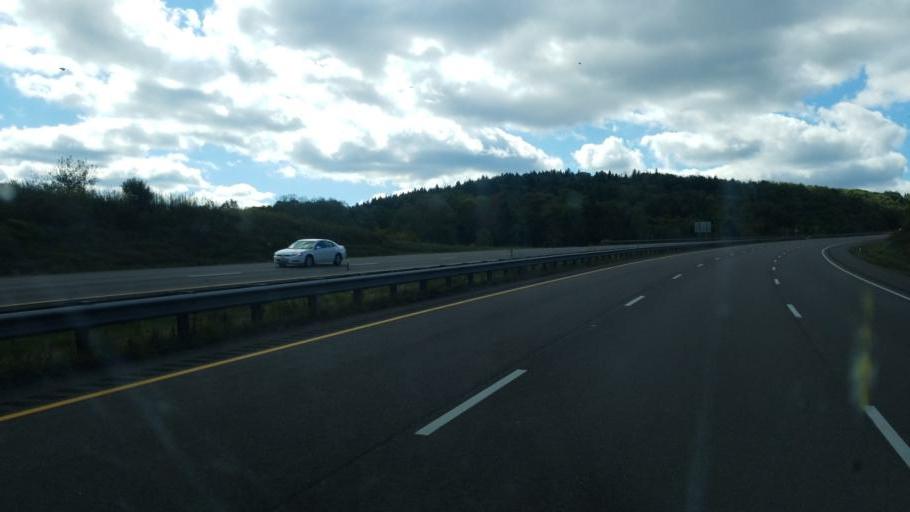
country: US
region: Maryland
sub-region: Allegany County
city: Frostburg
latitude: 39.6826
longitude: -79.0585
